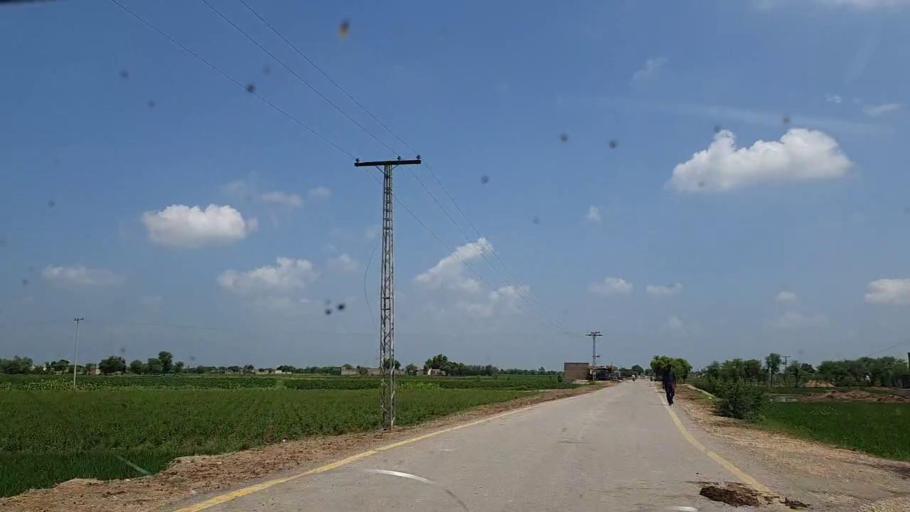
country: PK
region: Sindh
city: Tharu Shah
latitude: 26.9836
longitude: 68.0802
